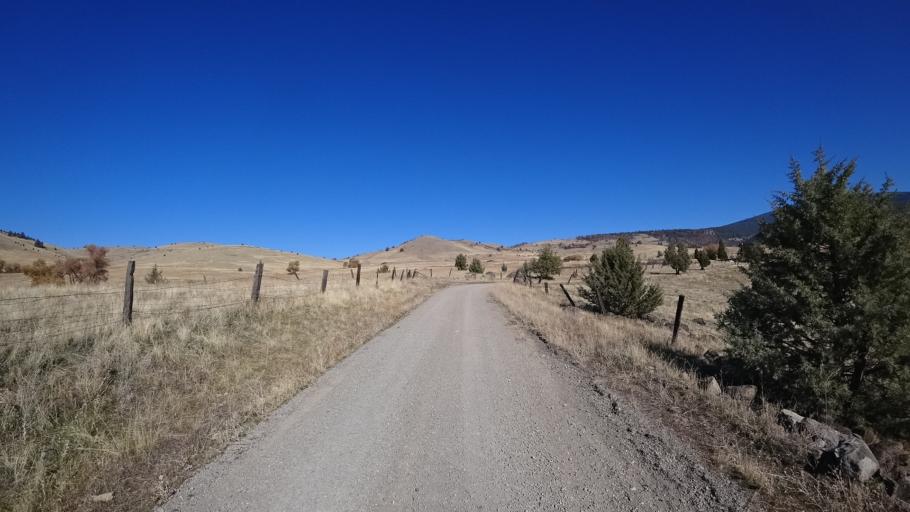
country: US
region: California
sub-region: Siskiyou County
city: Montague
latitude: 41.7985
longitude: -122.3346
